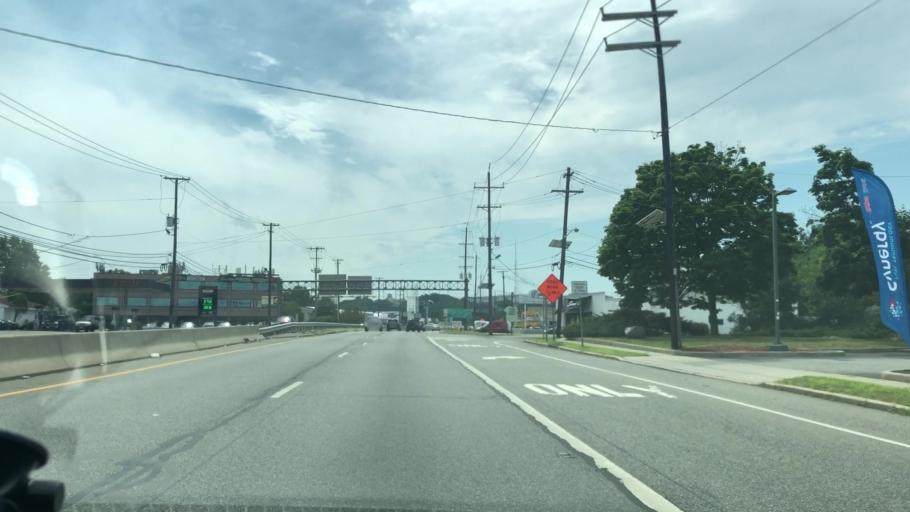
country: US
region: New Jersey
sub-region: Passaic County
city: Clifton
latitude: 40.8712
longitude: -74.1800
